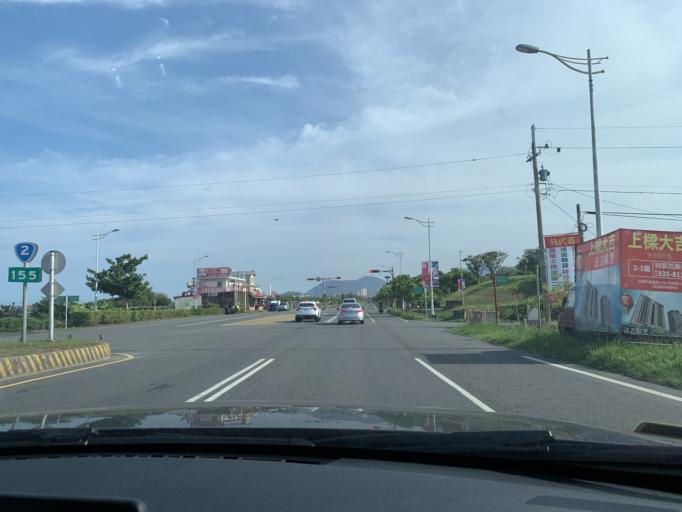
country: TW
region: Taiwan
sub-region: Yilan
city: Yilan
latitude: 24.6889
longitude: 121.8254
